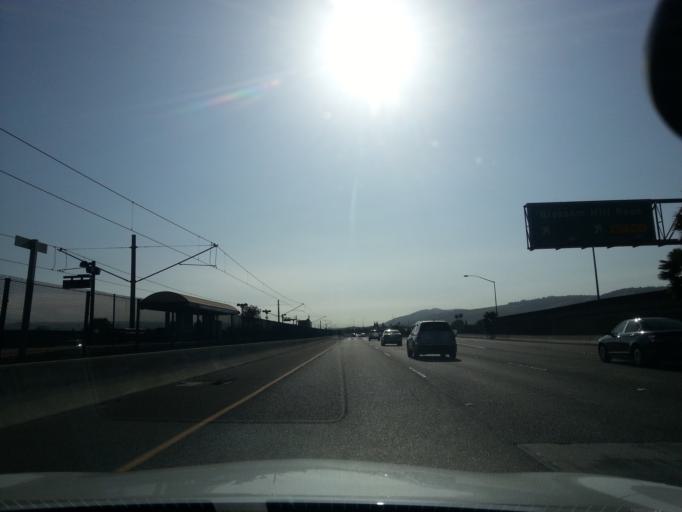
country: US
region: California
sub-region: Santa Clara County
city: Seven Trees
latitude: 37.2532
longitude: -121.8422
